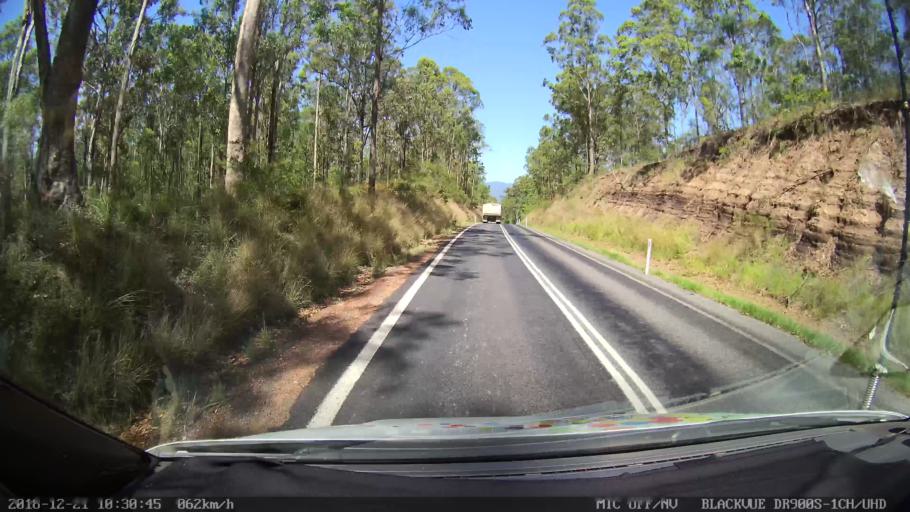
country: AU
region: New South Wales
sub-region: Clarence Valley
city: South Grafton
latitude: -29.6330
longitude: 152.7049
